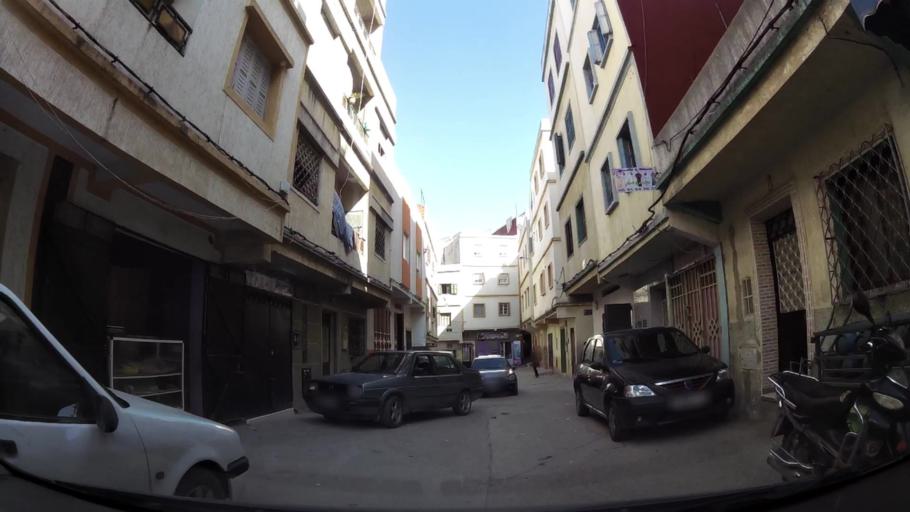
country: MA
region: Tanger-Tetouan
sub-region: Tanger-Assilah
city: Tangier
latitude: 35.7491
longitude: -5.8029
